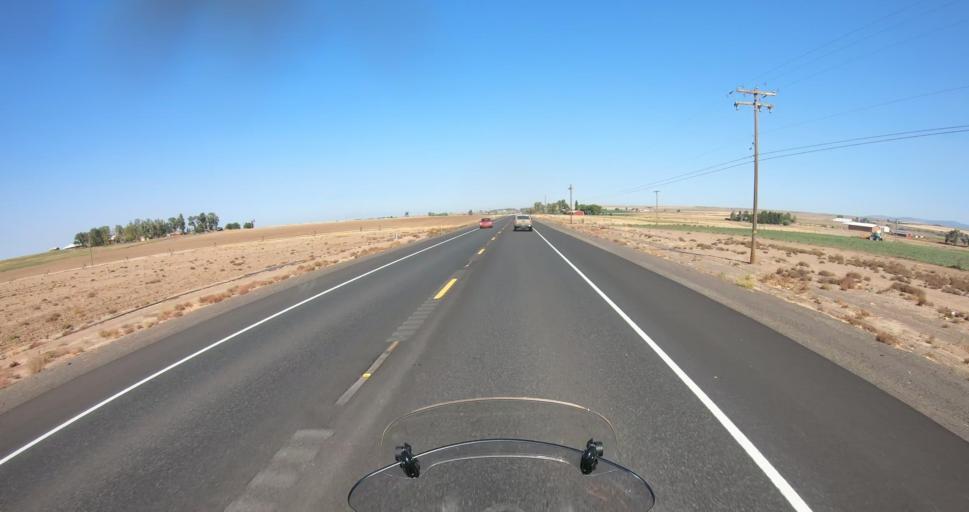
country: US
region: Oregon
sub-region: Jefferson County
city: Culver
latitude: 44.5401
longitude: -121.1698
